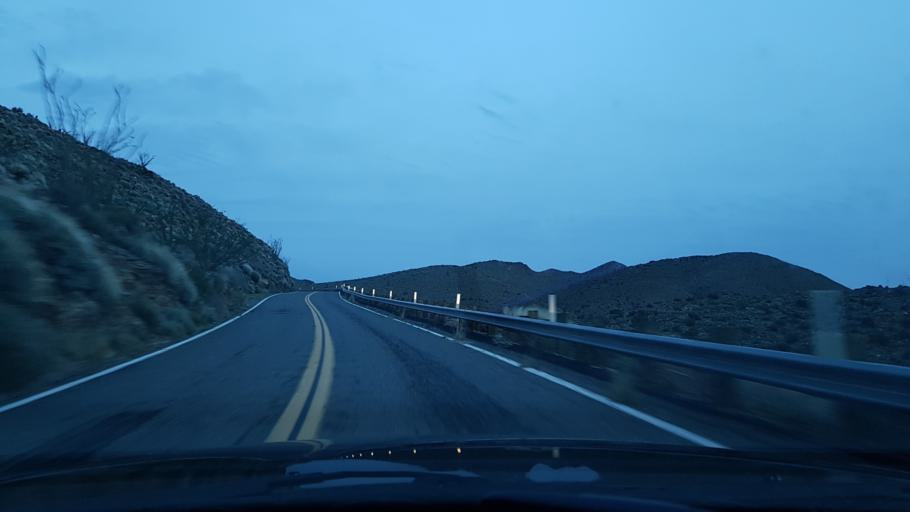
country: US
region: California
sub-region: San Diego County
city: Julian
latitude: 33.0146
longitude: -116.4466
